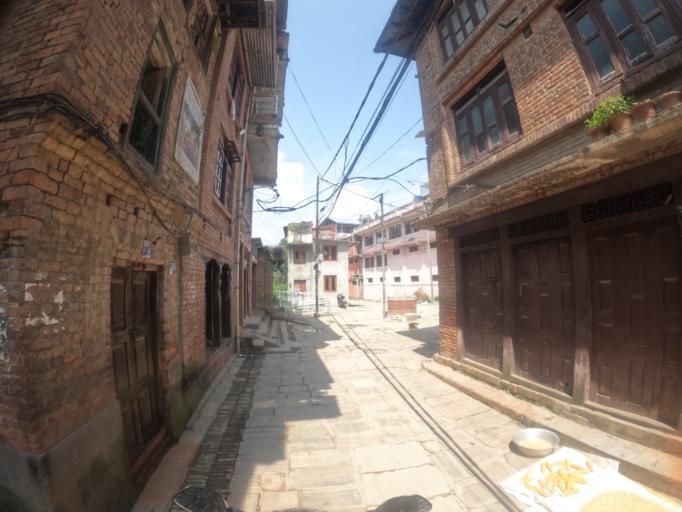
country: NP
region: Central Region
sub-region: Bagmati Zone
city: Bhaktapur
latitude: 27.6912
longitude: 85.3873
